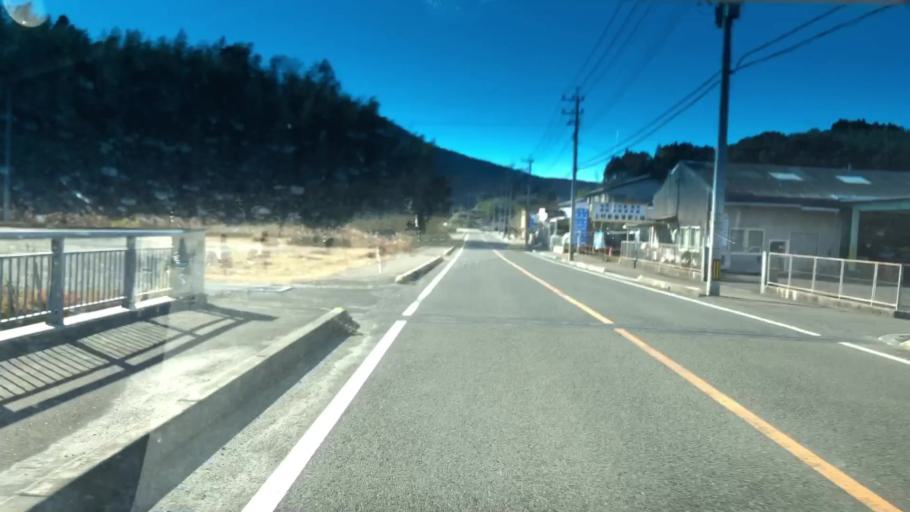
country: JP
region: Kagoshima
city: Satsumasendai
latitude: 31.8172
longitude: 130.2776
